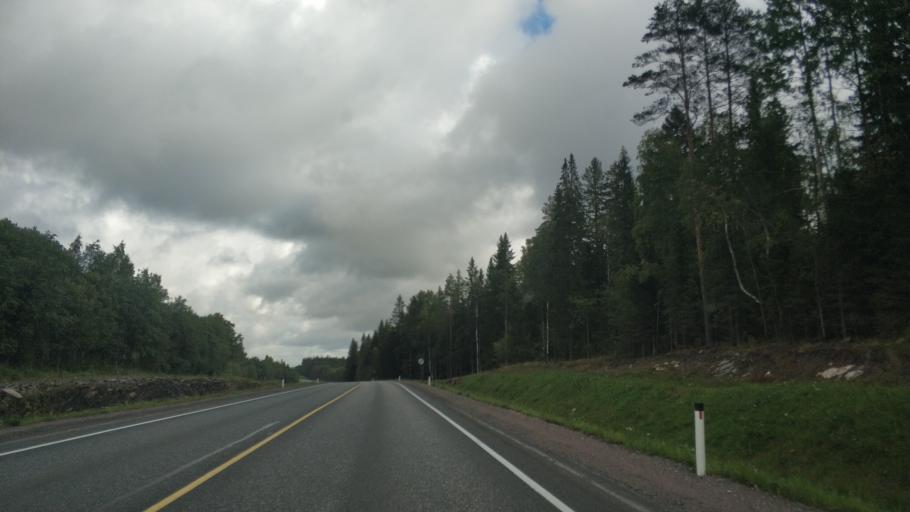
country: RU
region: Republic of Karelia
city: Khelyulya
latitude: 61.8493
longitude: 30.6497
